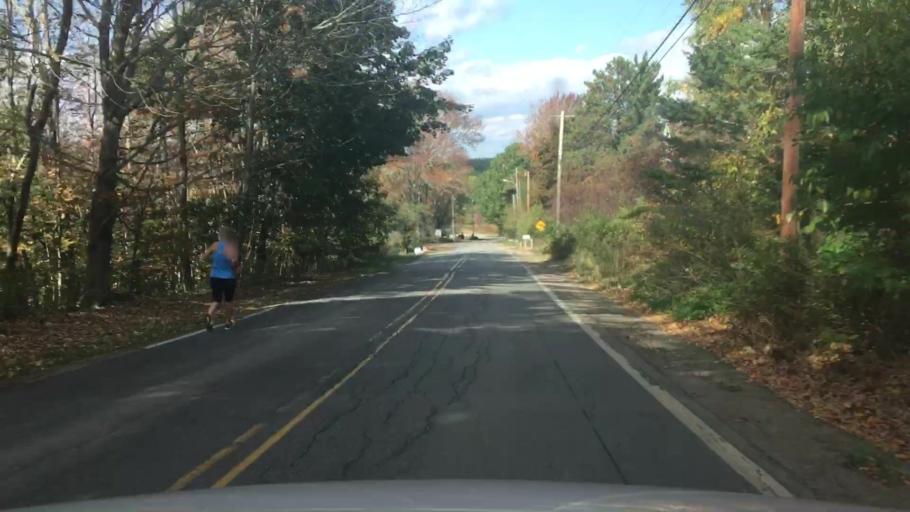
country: US
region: Maine
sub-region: Knox County
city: Union
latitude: 44.1951
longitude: -69.2634
